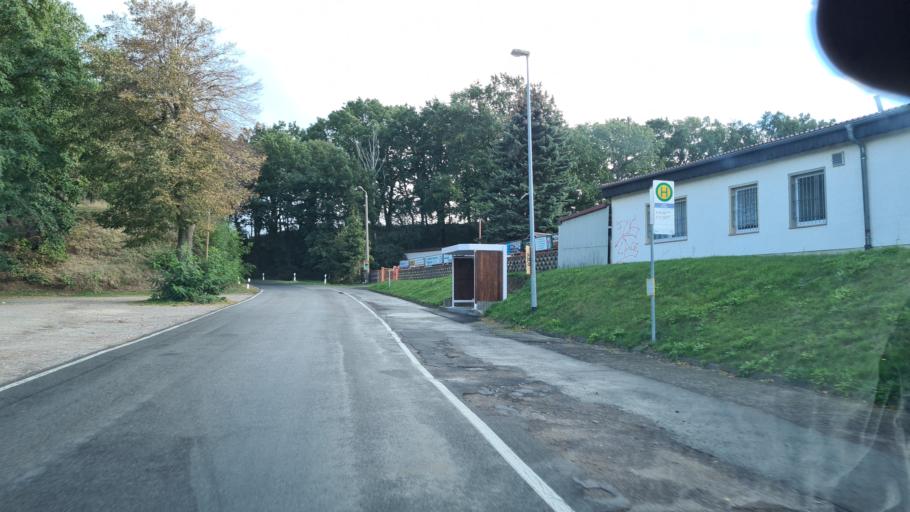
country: DE
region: Saxony
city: Dahlen
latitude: 51.3642
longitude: 13.0089
